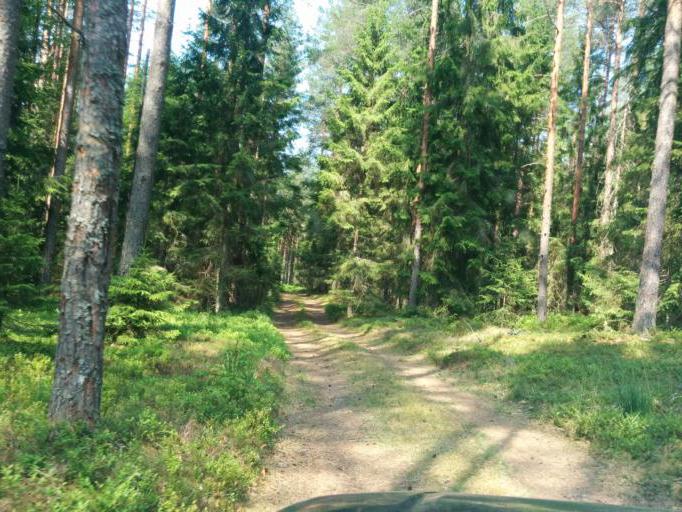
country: LV
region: Ikskile
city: Ikskile
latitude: 56.7422
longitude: 24.5029
